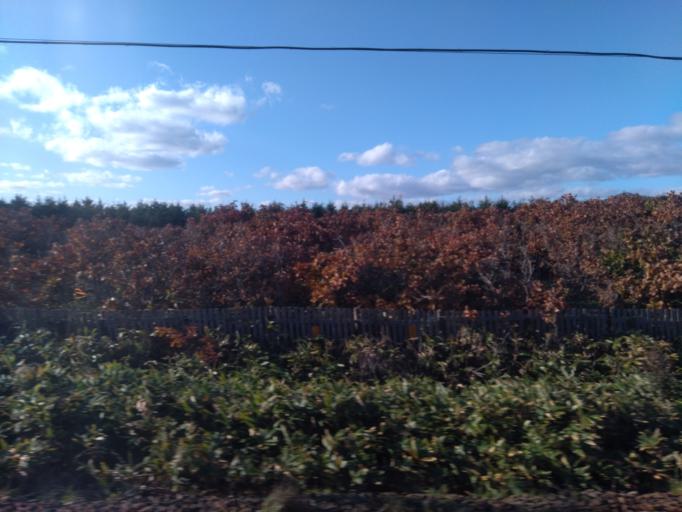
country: JP
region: Hokkaido
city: Niseko Town
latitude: 42.5442
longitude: 140.4103
